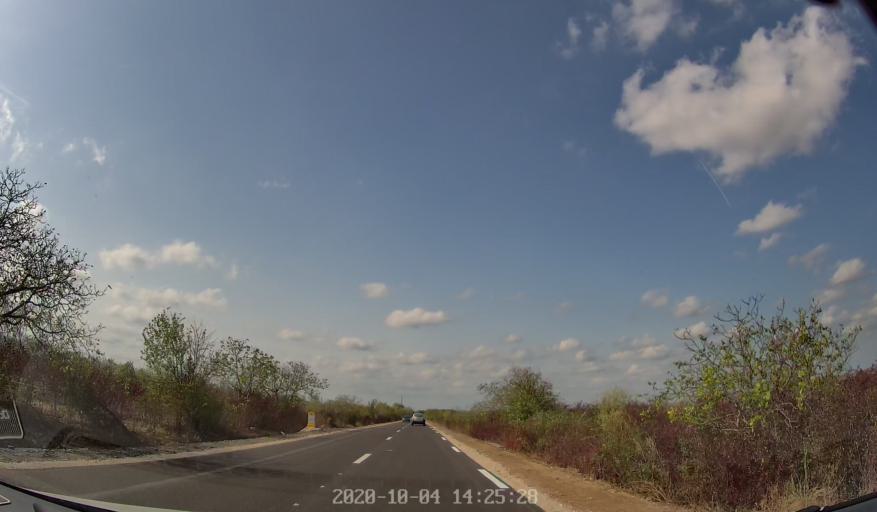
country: MD
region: Rezina
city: Saharna
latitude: 47.6206
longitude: 28.8984
